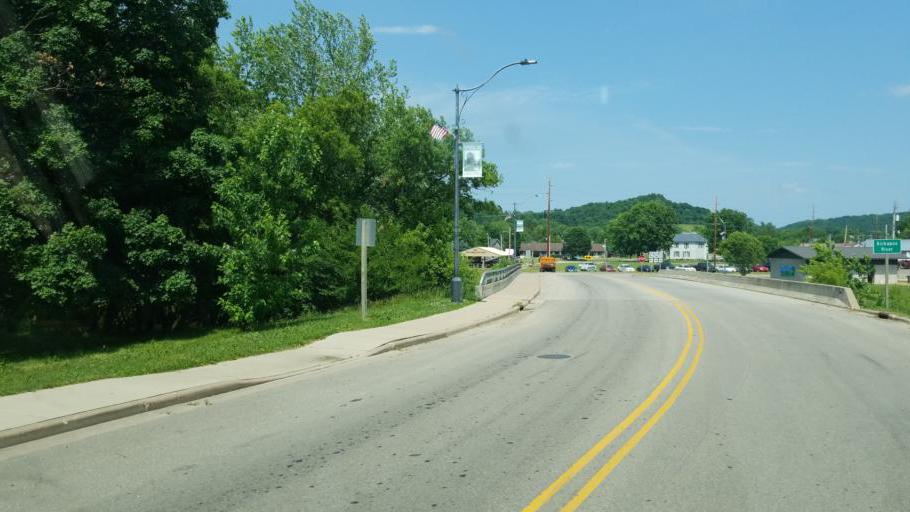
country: US
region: Wisconsin
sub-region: Vernon County
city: Viroqua
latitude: 43.5059
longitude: -90.6744
